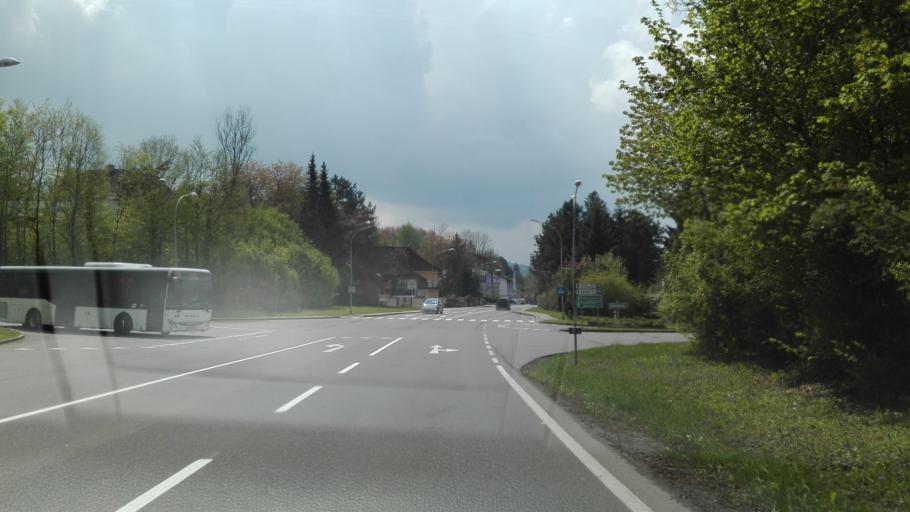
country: AT
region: Upper Austria
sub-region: Politischer Bezirk Steyr-Land
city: Sankt Ulrich bei Steyr
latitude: 48.0276
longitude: 14.4189
